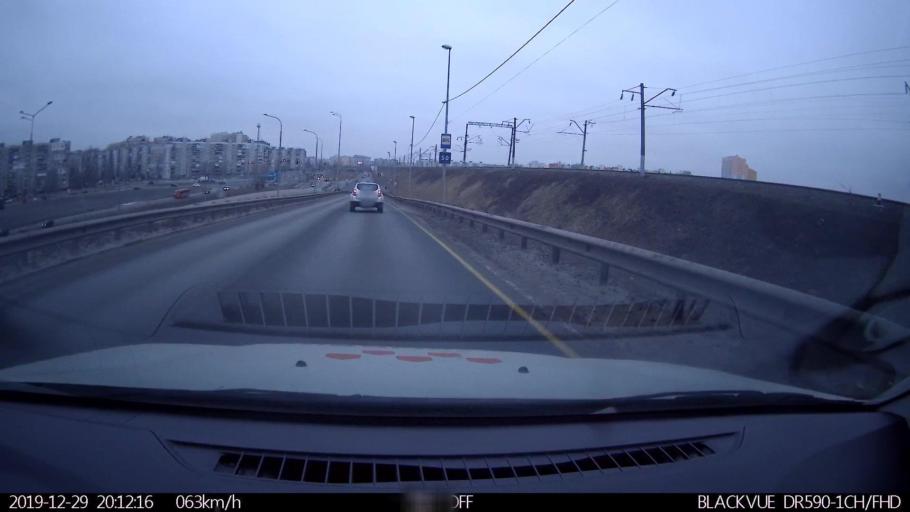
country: RU
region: Nizjnij Novgorod
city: Nizhniy Novgorod
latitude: 56.3479
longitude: 43.9214
